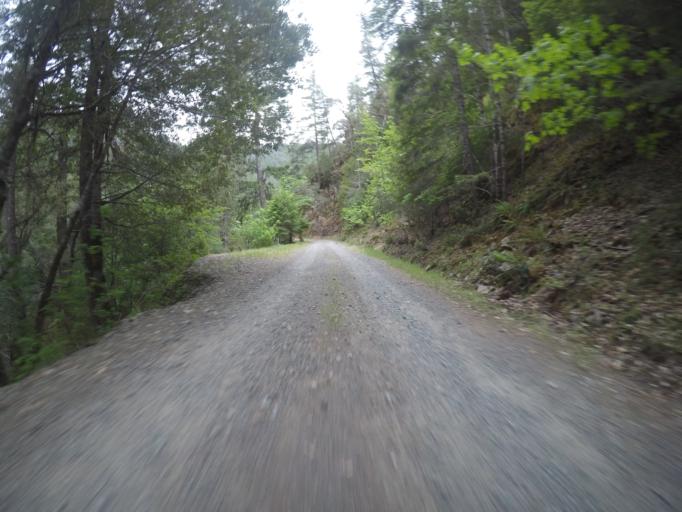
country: US
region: California
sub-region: Del Norte County
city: Bertsch-Oceanview
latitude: 41.7401
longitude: -123.8793
